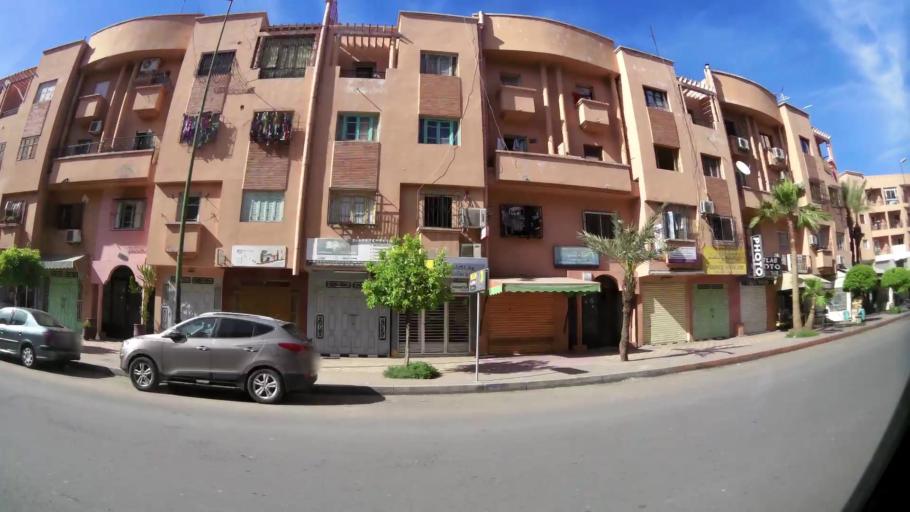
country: MA
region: Marrakech-Tensift-Al Haouz
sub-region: Marrakech
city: Marrakesh
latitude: 31.6488
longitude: -8.0101
